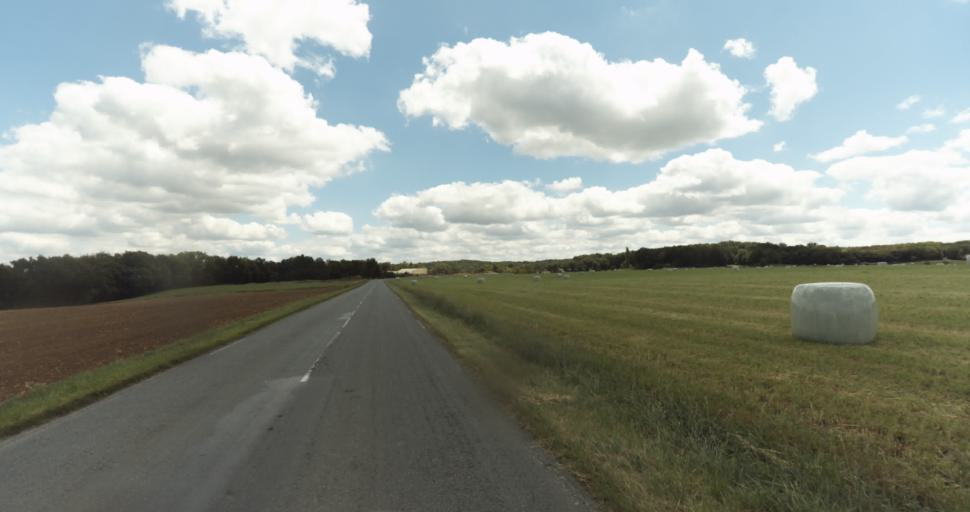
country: FR
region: Aquitaine
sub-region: Departement de la Dordogne
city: Beaumont-du-Perigord
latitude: 44.7146
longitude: 0.8057
